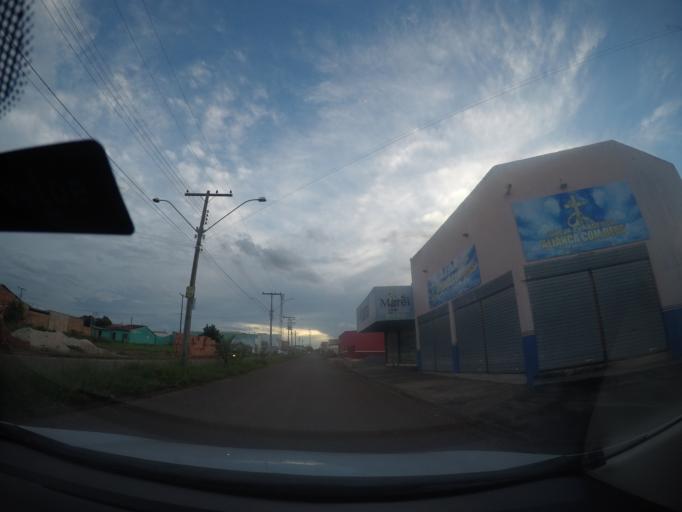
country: BR
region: Goias
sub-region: Goianira
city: Goianira
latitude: -16.5721
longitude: -49.3805
